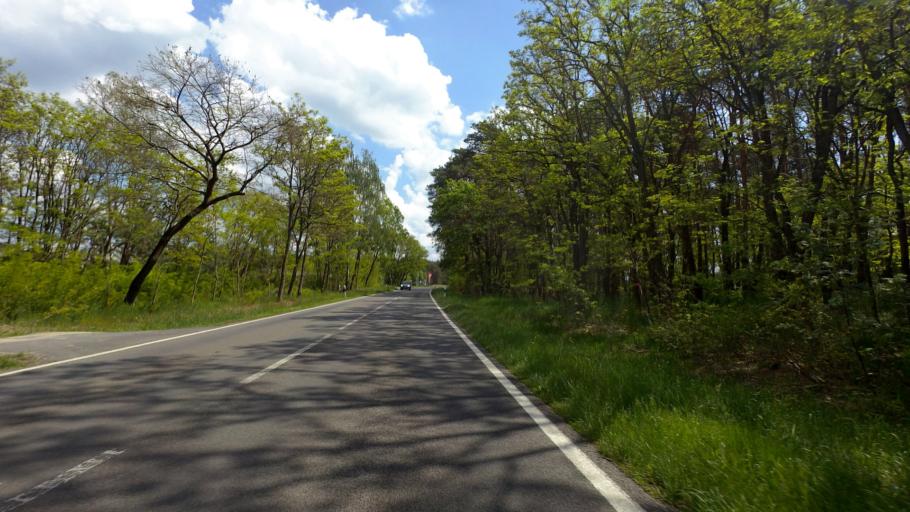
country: DE
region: Brandenburg
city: Luebben
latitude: 51.9449
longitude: 13.9565
